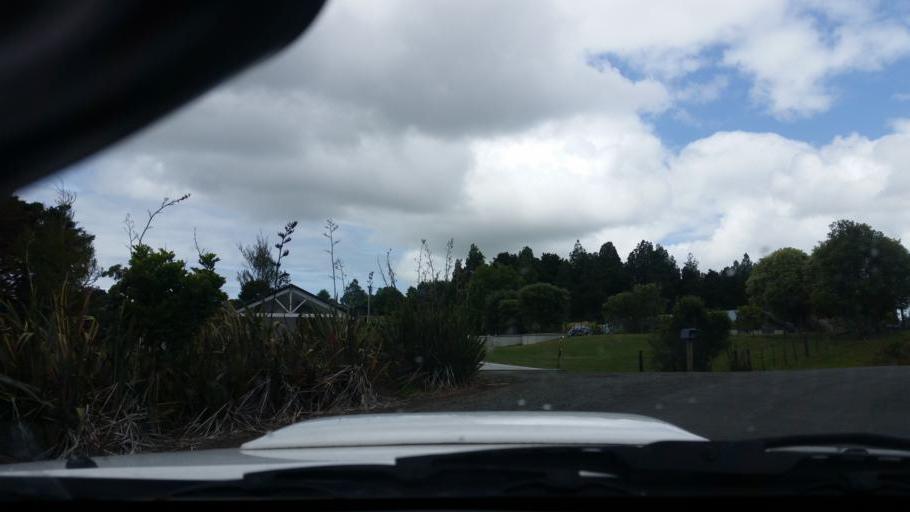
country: NZ
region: Northland
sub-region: Whangarei
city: Ruakaka
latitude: -36.0971
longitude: 174.3522
